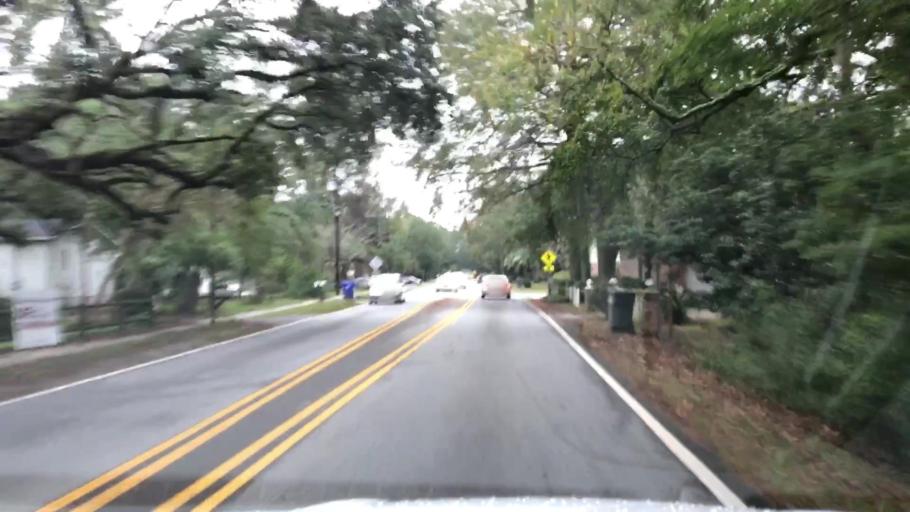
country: US
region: South Carolina
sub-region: Charleston County
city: North Charleston
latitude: 32.8148
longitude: -80.0028
